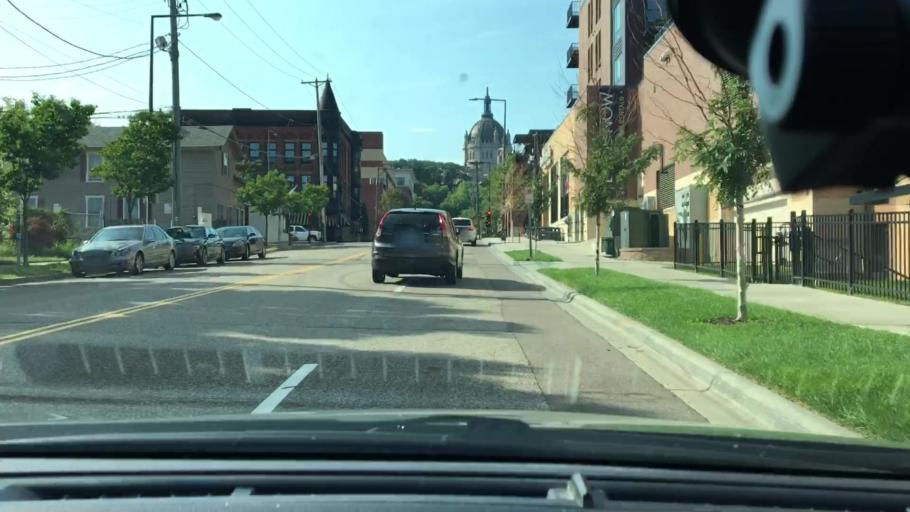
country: US
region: Minnesota
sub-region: Ramsey County
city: Saint Paul
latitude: 44.9429
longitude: -93.1032
